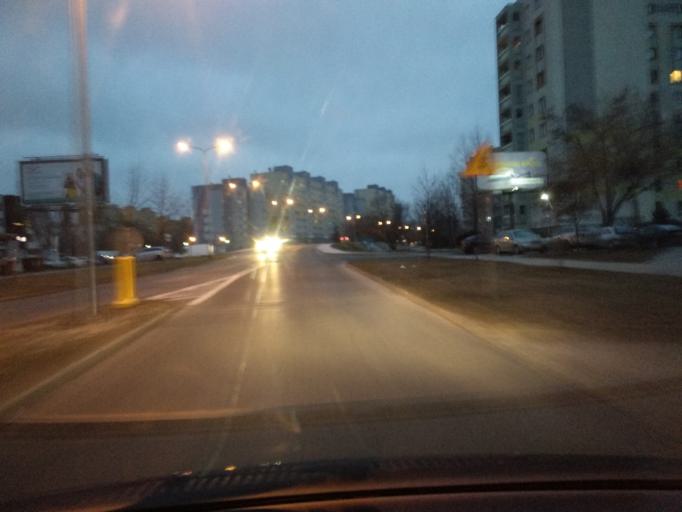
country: PL
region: Lower Silesian Voivodeship
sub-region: Powiat wroclawski
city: Wroclaw
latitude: 51.1268
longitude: 16.9631
